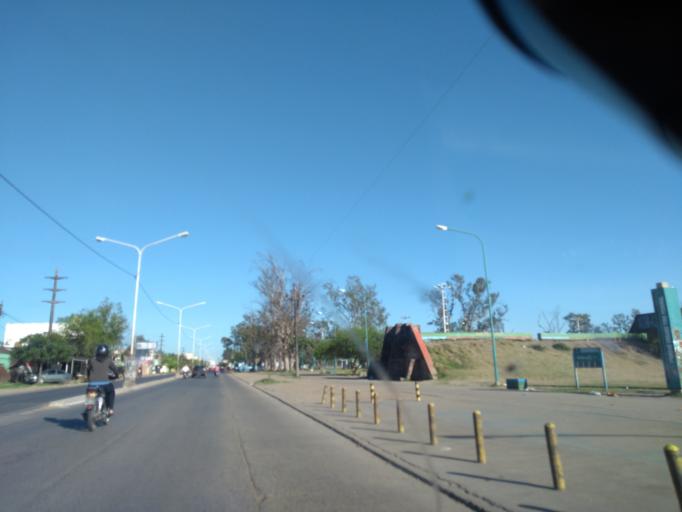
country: AR
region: Chaco
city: Resistencia
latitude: -27.4720
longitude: -58.9771
